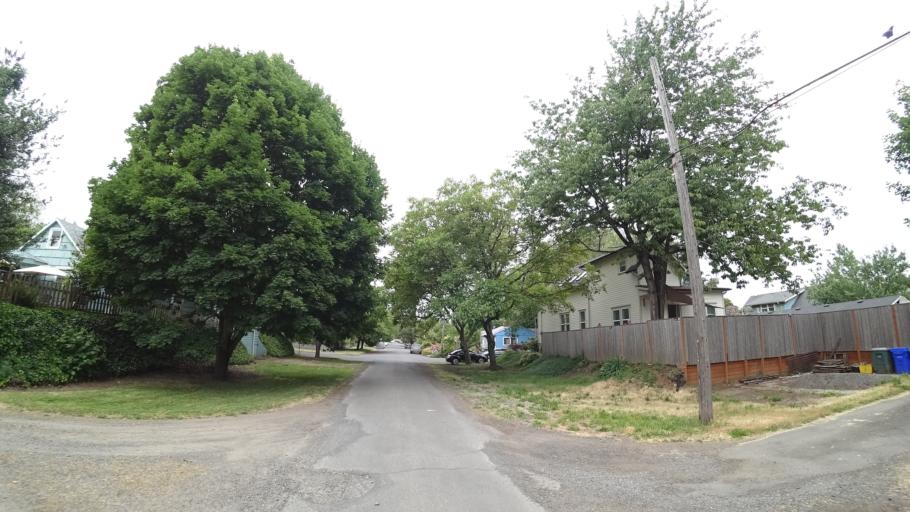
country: US
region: Oregon
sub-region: Multnomah County
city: Lents
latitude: 45.5148
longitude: -122.5833
